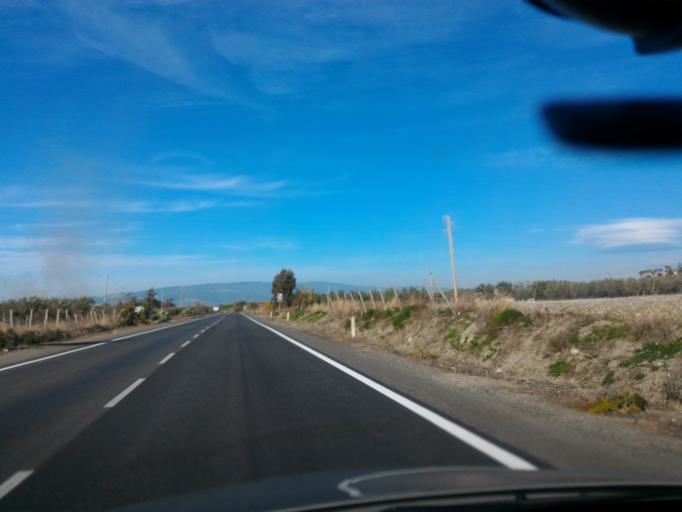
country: IT
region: Calabria
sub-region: Provincia di Crotone
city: Le Castella
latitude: 38.9354
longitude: 17.0061
